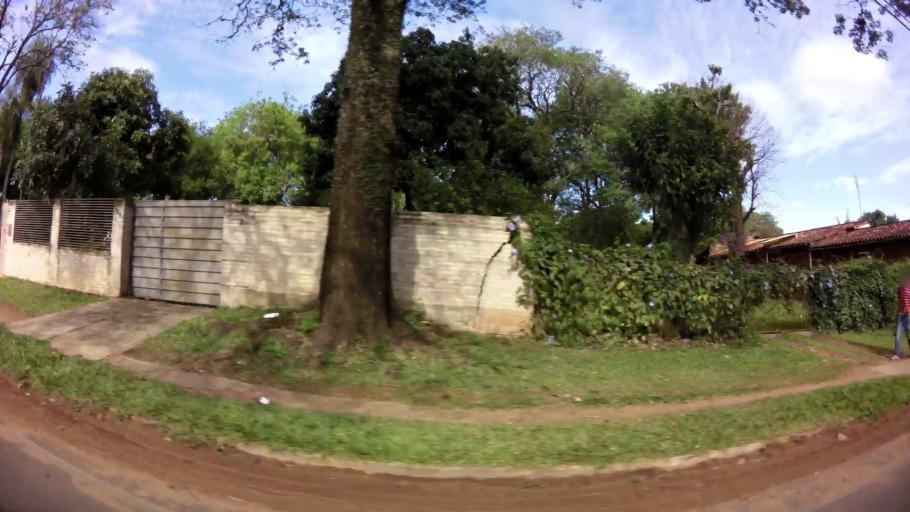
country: PY
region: Central
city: San Lorenzo
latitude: -25.2783
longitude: -57.4854
